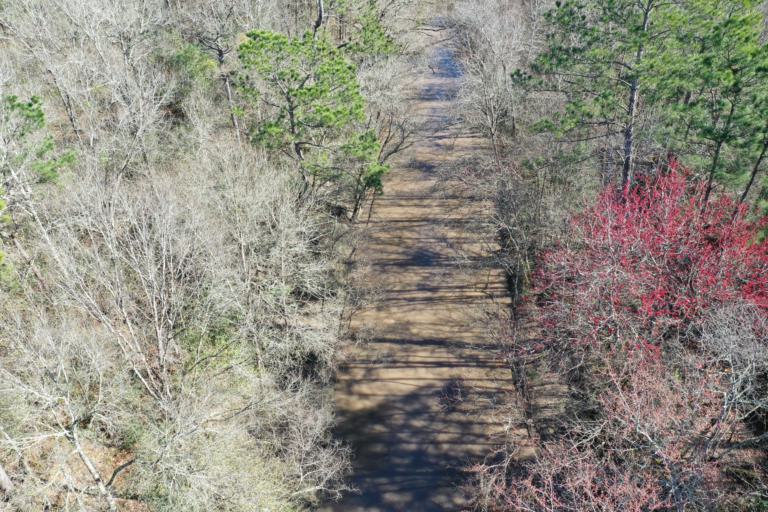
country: US
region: Louisiana
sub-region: Calcasieu Parish
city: Iowa
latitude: 30.3167
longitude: -93.0330
